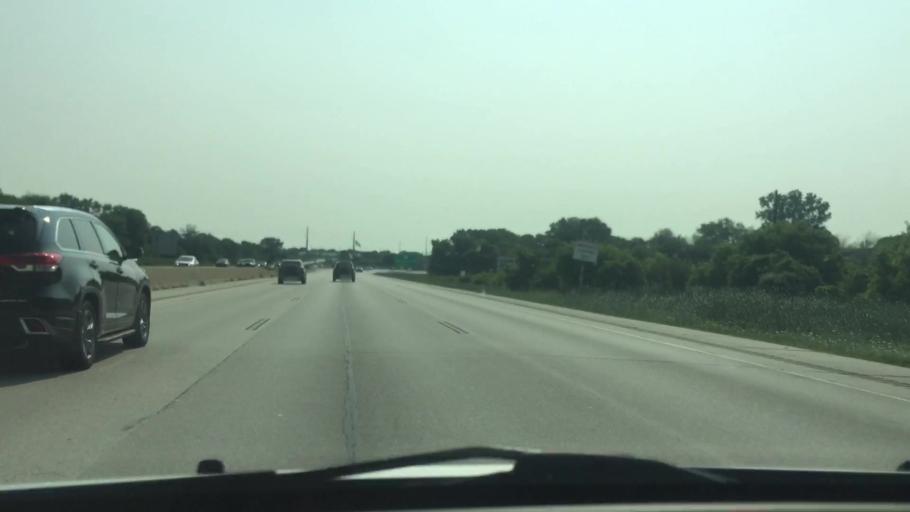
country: US
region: Wisconsin
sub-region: Waukesha County
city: Waukesha
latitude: 43.0488
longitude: -88.2164
